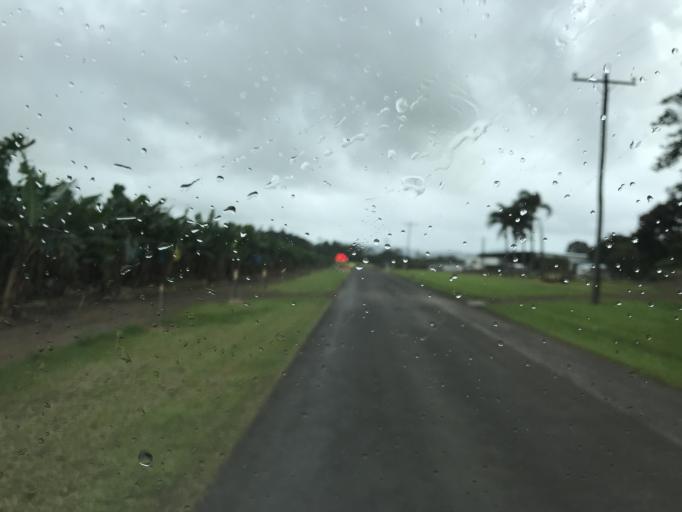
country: AU
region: Queensland
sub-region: Cassowary Coast
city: Innisfail
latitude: -17.5037
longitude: 145.9806
